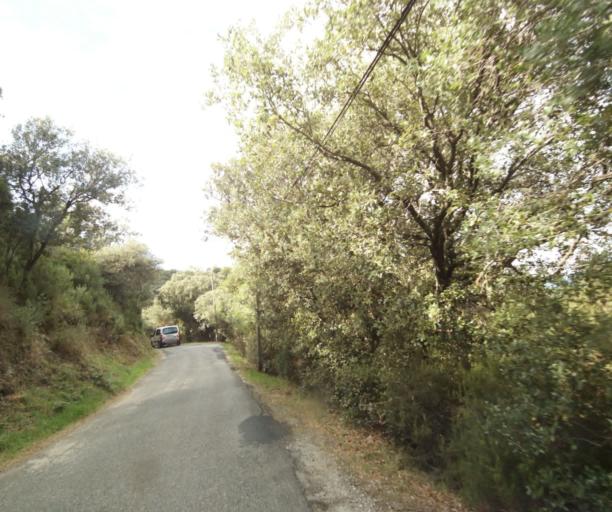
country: FR
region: Languedoc-Roussillon
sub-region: Departement des Pyrenees-Orientales
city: Sorede
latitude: 42.5236
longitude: 2.9868
